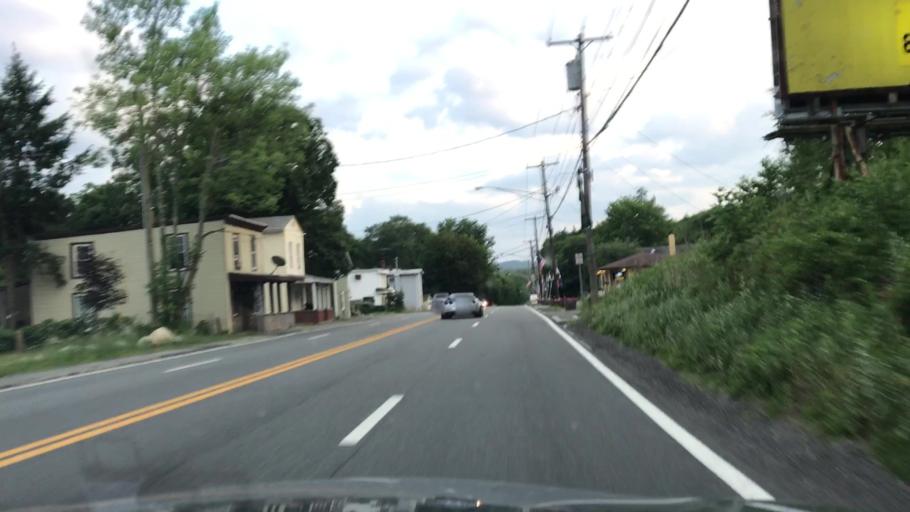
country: US
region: New York
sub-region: Rockland County
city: Sloatsburg
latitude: 41.1764
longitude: -74.1875
